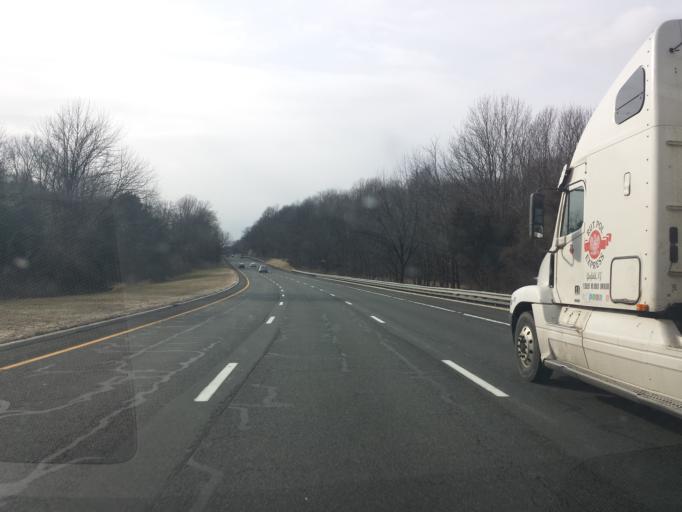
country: US
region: New Jersey
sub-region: Warren County
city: Hackettstown
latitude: 40.9306
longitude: -74.9050
